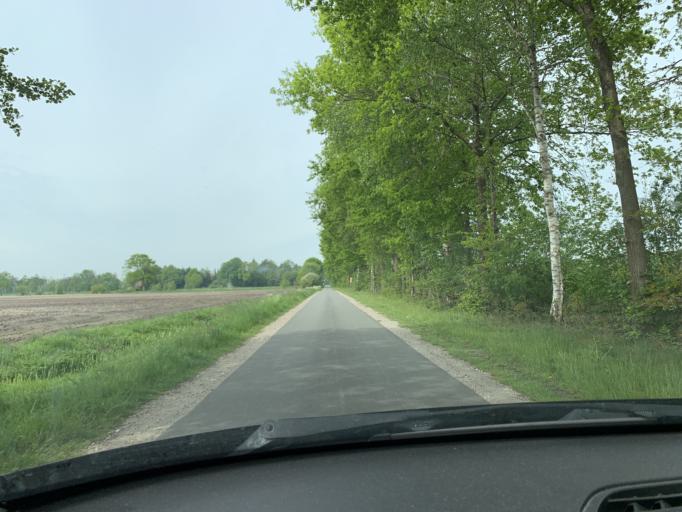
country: DE
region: Lower Saxony
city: Apen
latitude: 53.2098
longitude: 7.7680
